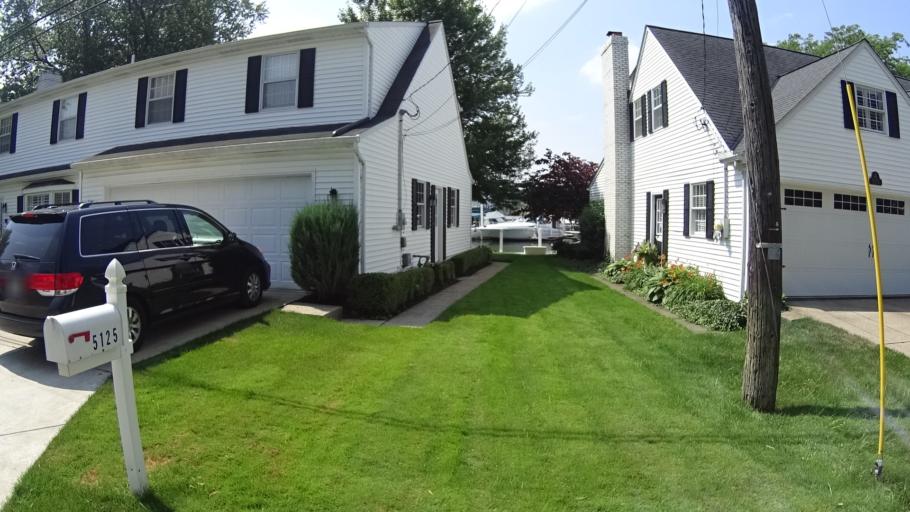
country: US
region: Ohio
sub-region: Lorain County
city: Vermilion
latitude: 41.4241
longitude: -82.3582
